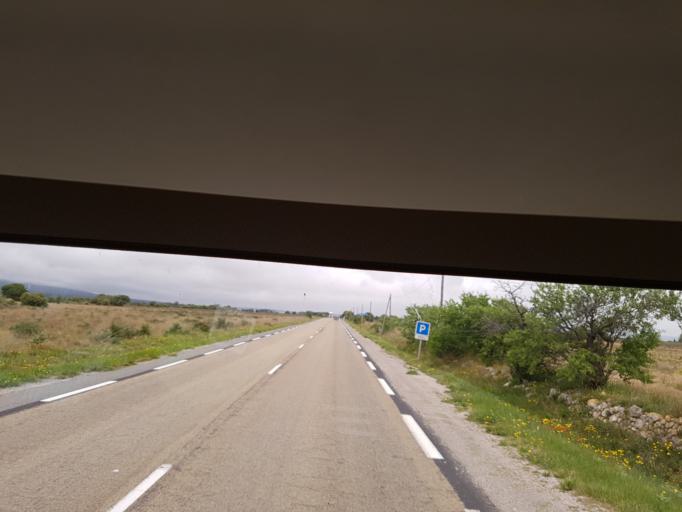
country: FR
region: Languedoc-Roussillon
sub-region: Departement de l'Aude
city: Leucate
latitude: 42.9220
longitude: 2.9956
